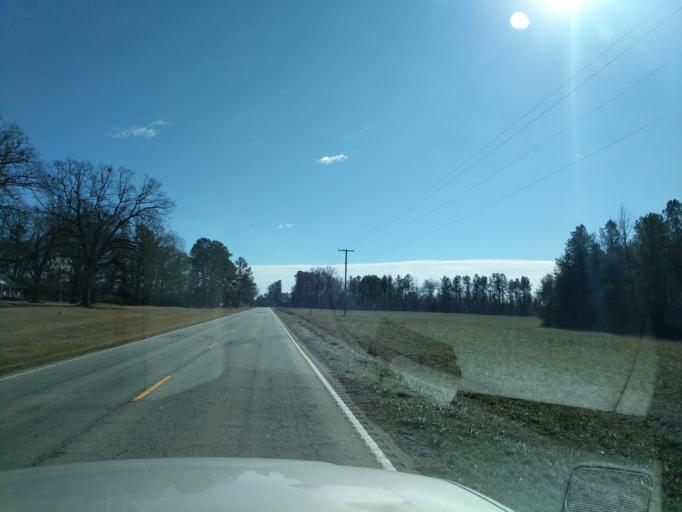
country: US
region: South Carolina
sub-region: Greenwood County
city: Ninety Six
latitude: 34.1953
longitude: -81.8811
